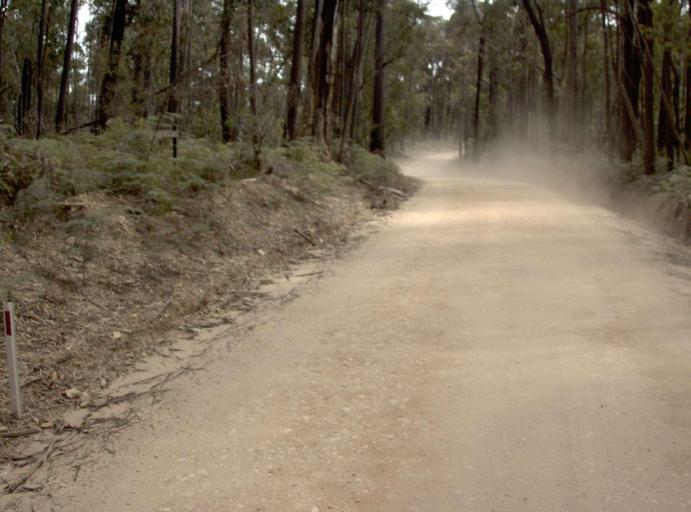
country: AU
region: Victoria
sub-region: East Gippsland
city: Lakes Entrance
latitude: -37.6809
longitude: 148.6247
